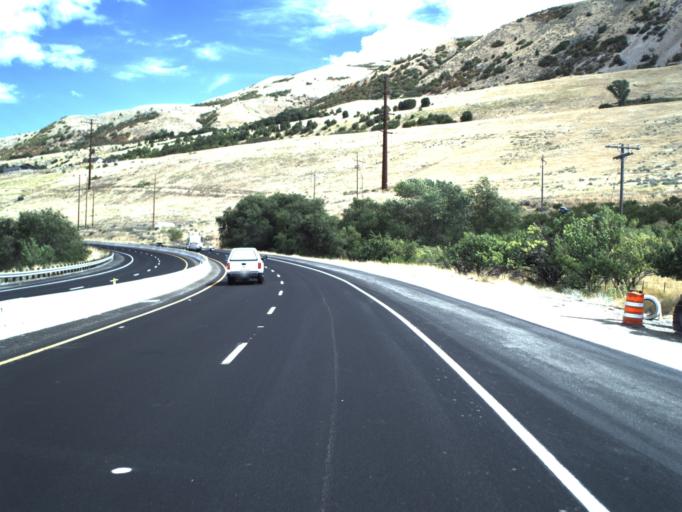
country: US
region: Utah
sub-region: Box Elder County
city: Brigham City
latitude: 41.4865
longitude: -112.0093
